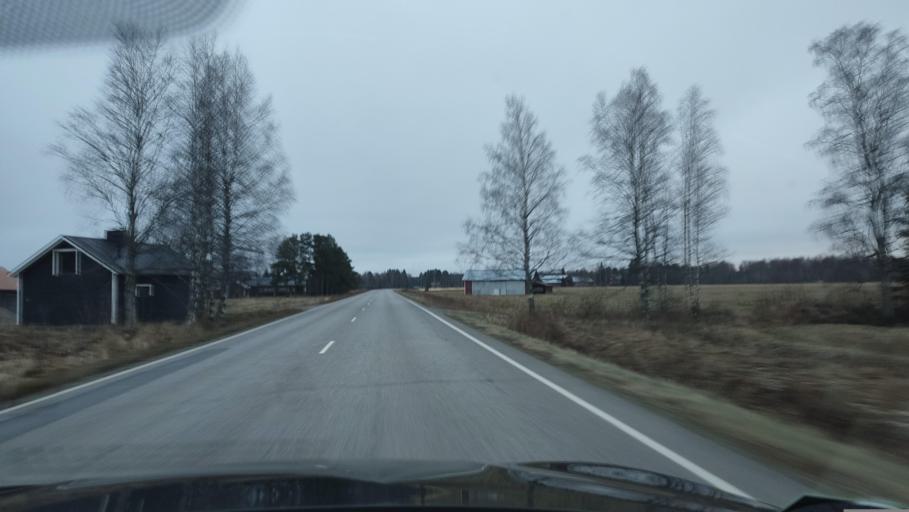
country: FI
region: Southern Ostrobothnia
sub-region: Suupohja
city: Kauhajoki
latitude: 62.3449
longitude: 22.0245
